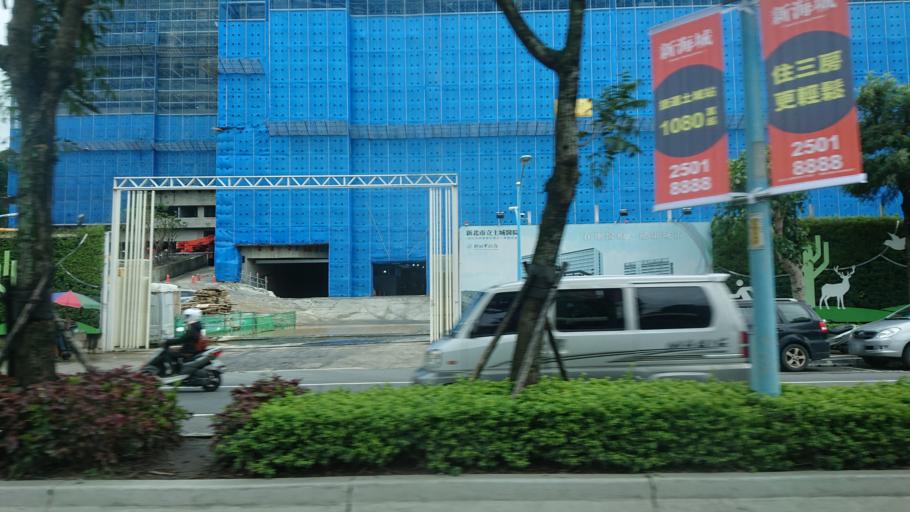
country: TW
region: Taipei
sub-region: Taipei
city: Banqiao
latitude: 24.9767
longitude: 121.4483
